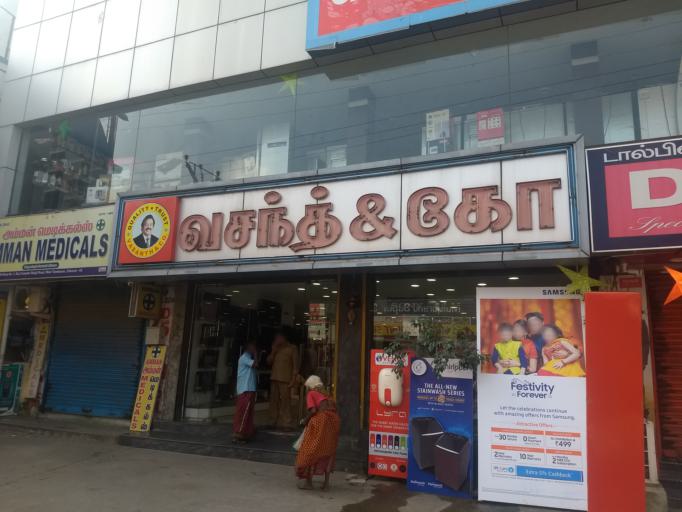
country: IN
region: Tamil Nadu
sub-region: Kancheepuram
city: Vandalur
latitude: 12.9285
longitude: 80.1155
